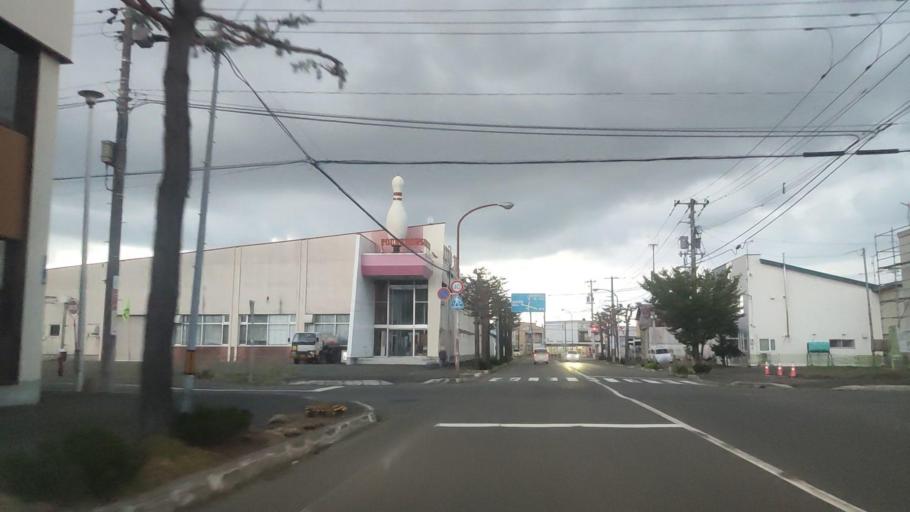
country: JP
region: Hokkaido
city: Shimo-furano
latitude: 43.3404
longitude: 142.3918
